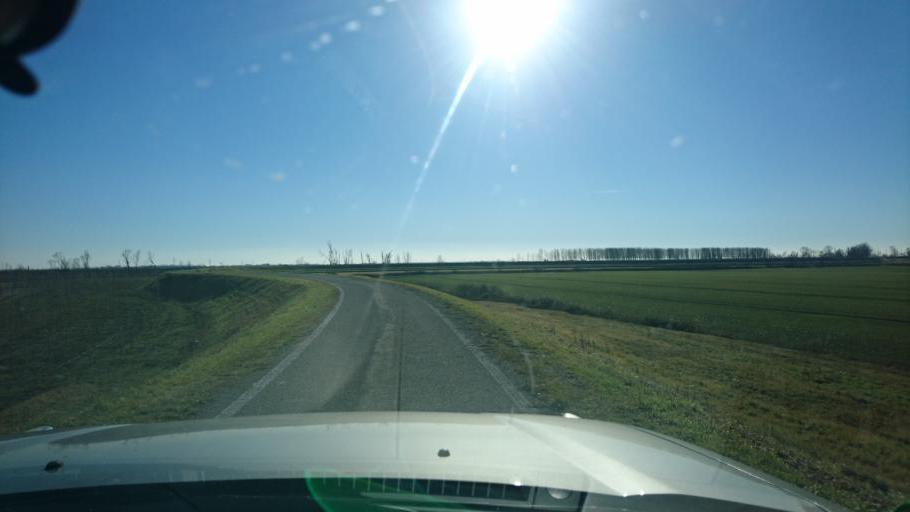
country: IT
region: Veneto
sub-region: Provincia di Rovigo
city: Ariano
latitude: 44.9355
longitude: 12.1575
